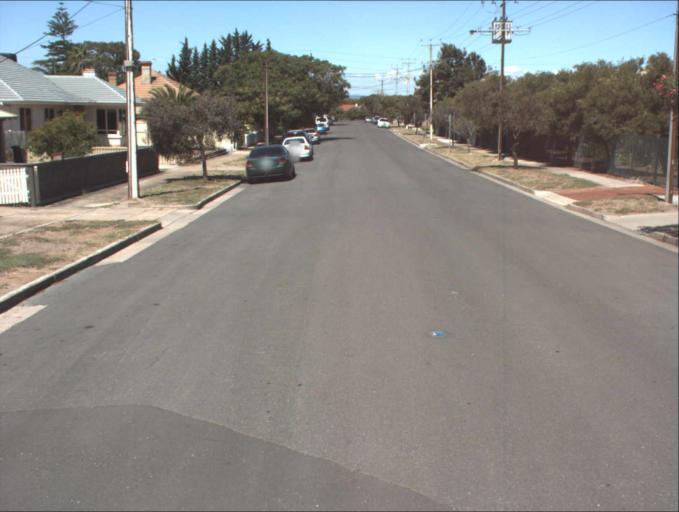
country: AU
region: South Australia
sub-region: Port Adelaide Enfield
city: Birkenhead
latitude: -34.8231
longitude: 138.4885
